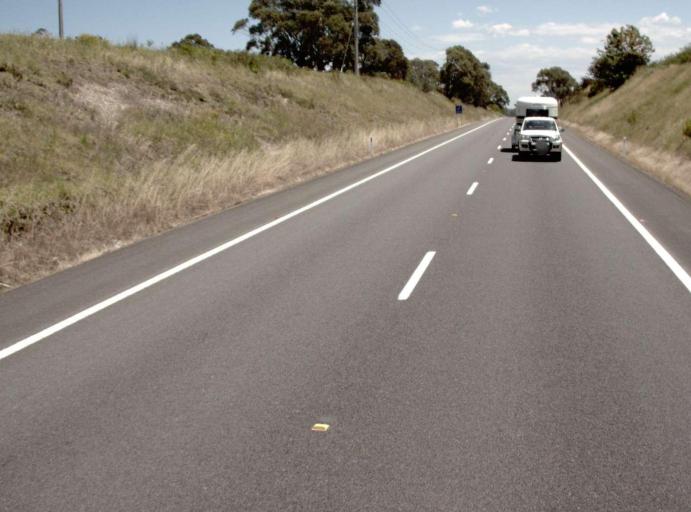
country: AU
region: Victoria
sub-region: East Gippsland
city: Lakes Entrance
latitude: -37.7030
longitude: 148.4766
